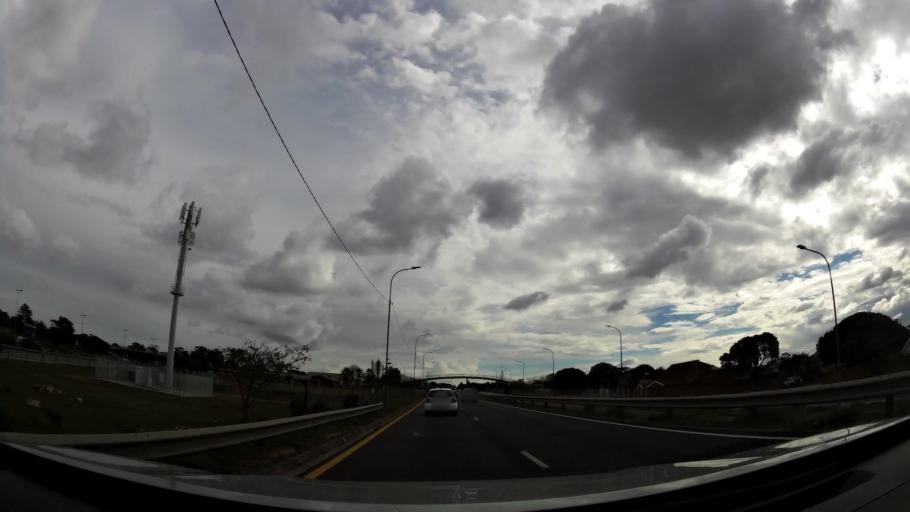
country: ZA
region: Eastern Cape
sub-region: Nelson Mandela Bay Metropolitan Municipality
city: Port Elizabeth
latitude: -33.9463
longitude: 25.5252
